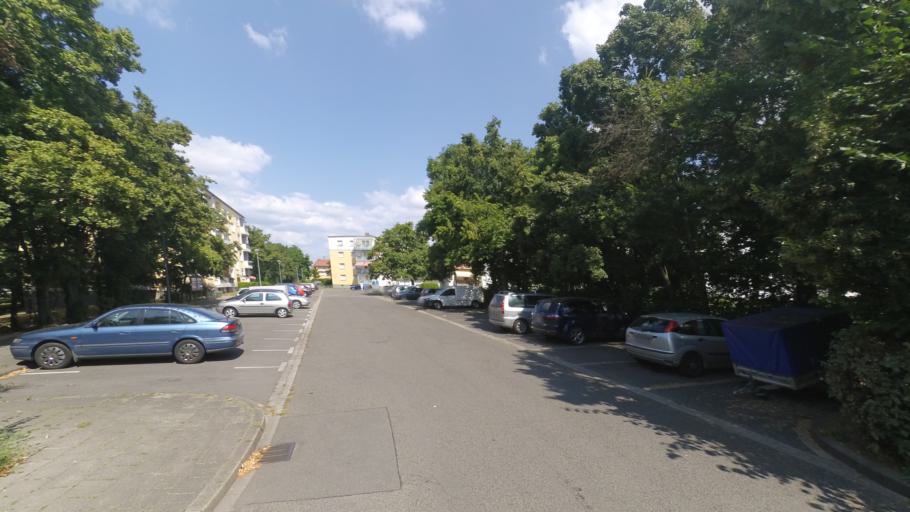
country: DE
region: Rheinland-Pfalz
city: Frankenthal
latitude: 49.5207
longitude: 8.3931
